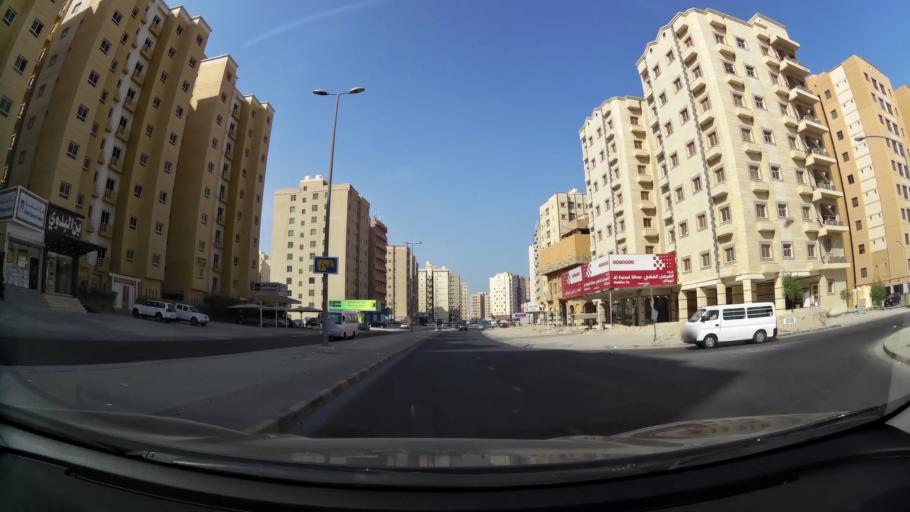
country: KW
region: Al Ahmadi
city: Al Mahbulah
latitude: 29.1546
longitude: 48.1161
